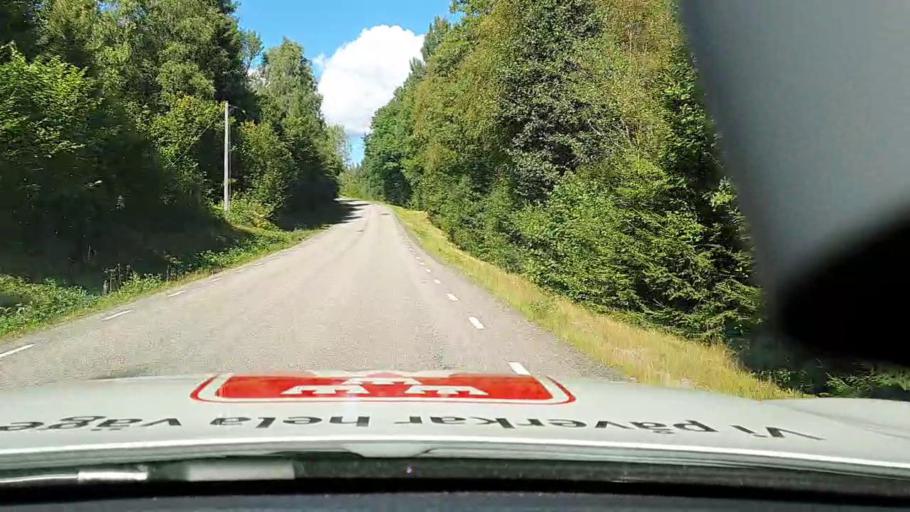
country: SE
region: Vaestra Goetaland
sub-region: Marks Kommun
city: Fritsla
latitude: 57.3724
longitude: 12.8616
